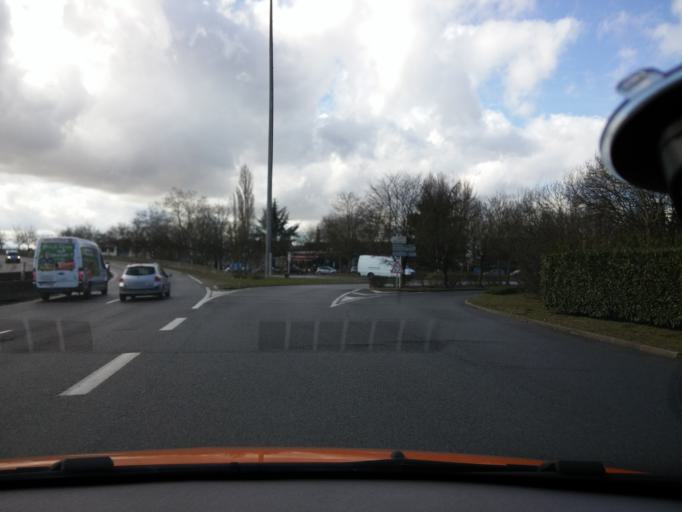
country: FR
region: Ile-de-France
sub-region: Departement de l'Essonne
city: Orsay
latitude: 48.6856
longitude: 2.2071
